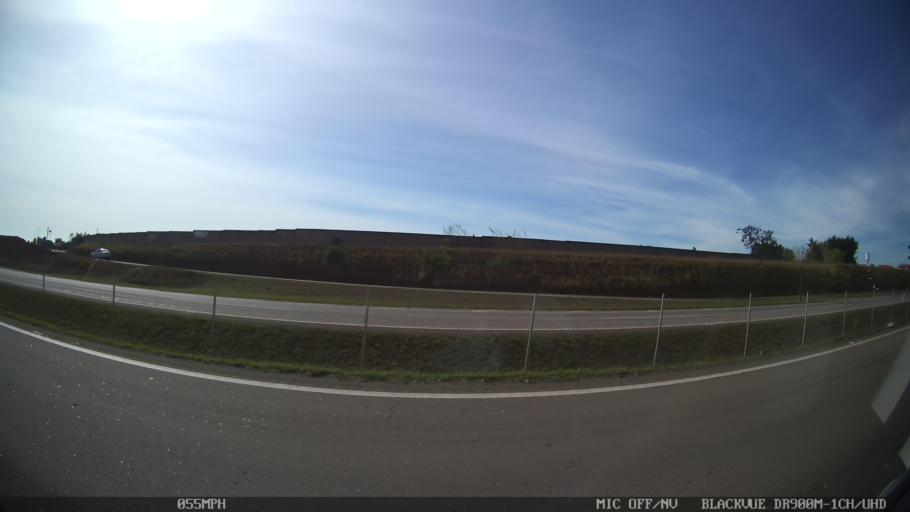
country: BR
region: Sao Paulo
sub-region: Piracicaba
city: Piracicaba
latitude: -22.7664
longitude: -47.5952
